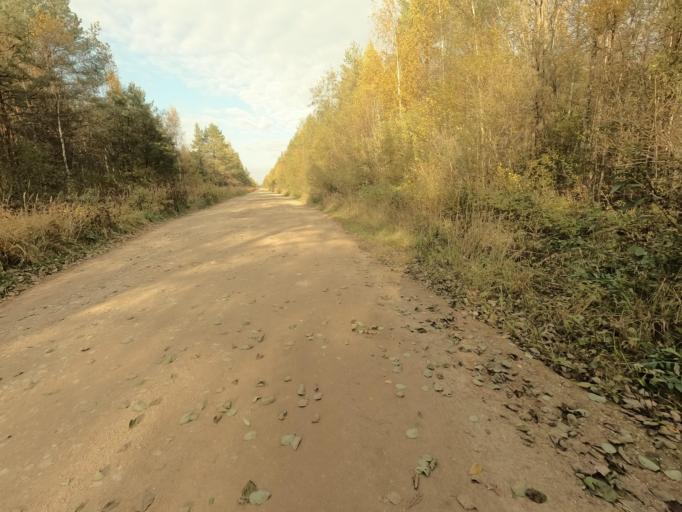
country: RU
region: Novgorod
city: Volkhovskiy
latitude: 58.8990
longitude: 31.0320
